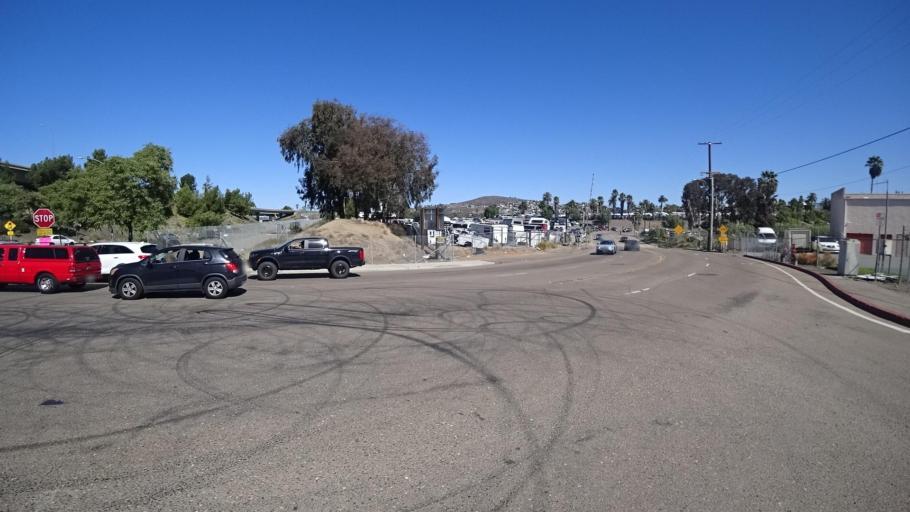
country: US
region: California
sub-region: San Diego County
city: La Presa
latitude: 32.7006
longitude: -117.0101
